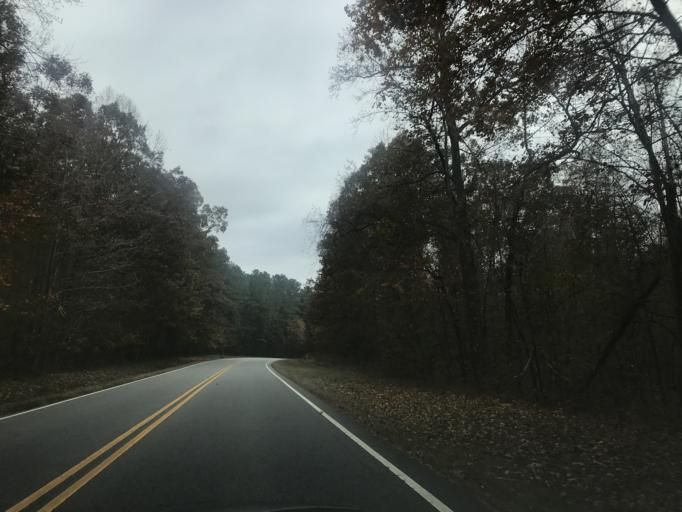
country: US
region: North Carolina
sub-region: Franklin County
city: Youngsville
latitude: 36.0083
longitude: -78.4905
